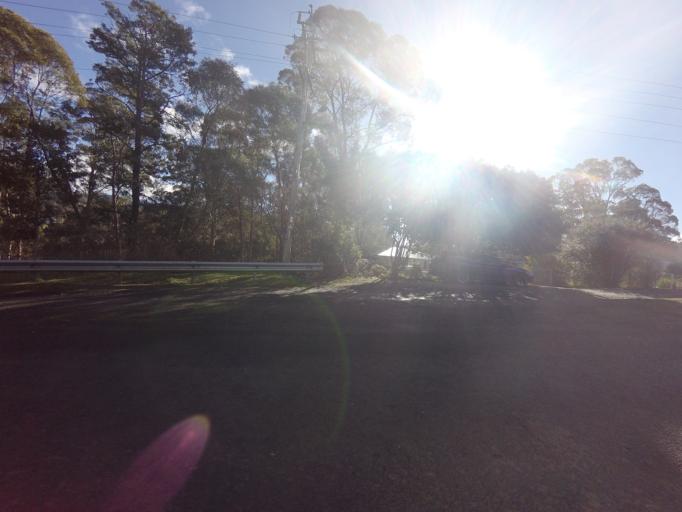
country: AU
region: Tasmania
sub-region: Glenorchy
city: Berriedale
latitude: -42.8431
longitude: 147.1917
